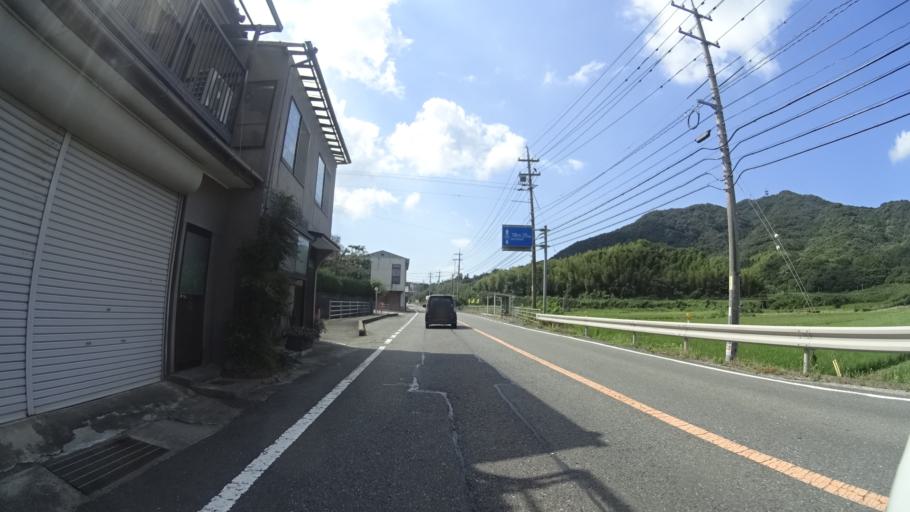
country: JP
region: Yamaguchi
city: Shimonoseki
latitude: 34.1123
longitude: 130.9038
